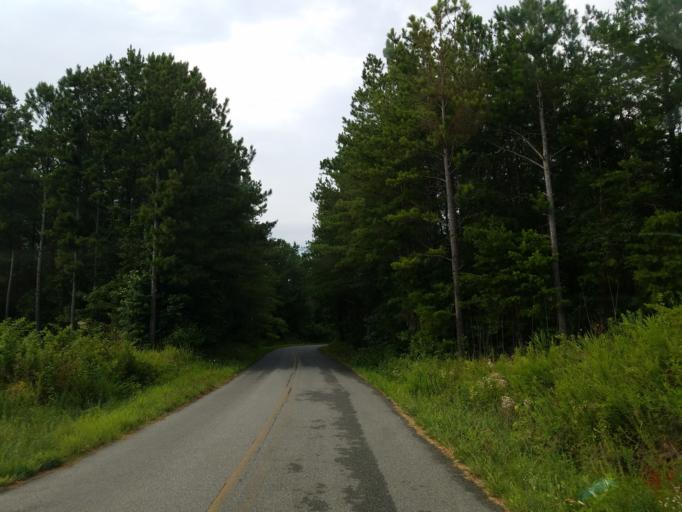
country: US
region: Georgia
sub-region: Bartow County
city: Rydal
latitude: 34.3838
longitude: -84.6681
